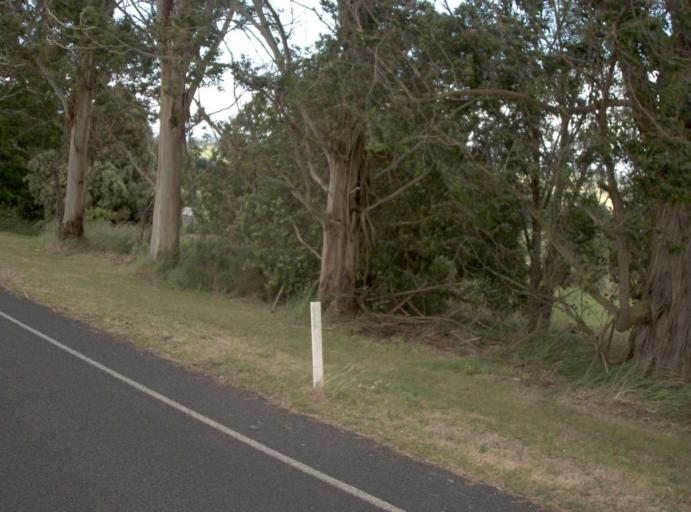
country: AU
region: Victoria
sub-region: Baw Baw
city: Warragul
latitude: -38.0979
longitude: 145.9217
